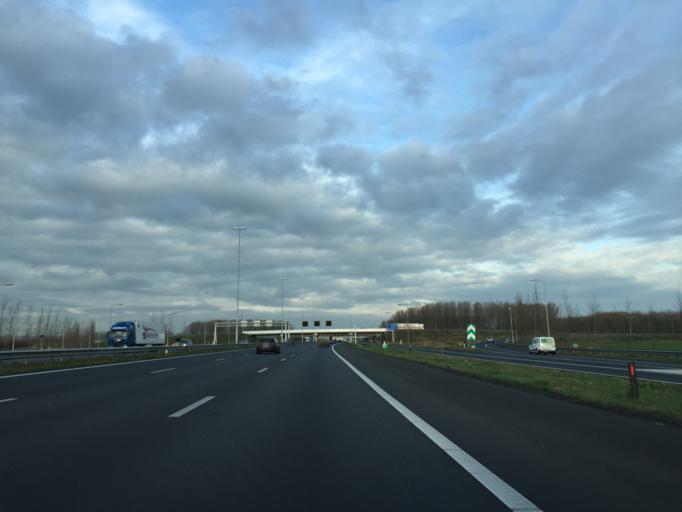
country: NL
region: Gelderland
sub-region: Gemeente Zaltbommel
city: Zaltbommel
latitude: 51.8526
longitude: 5.2327
